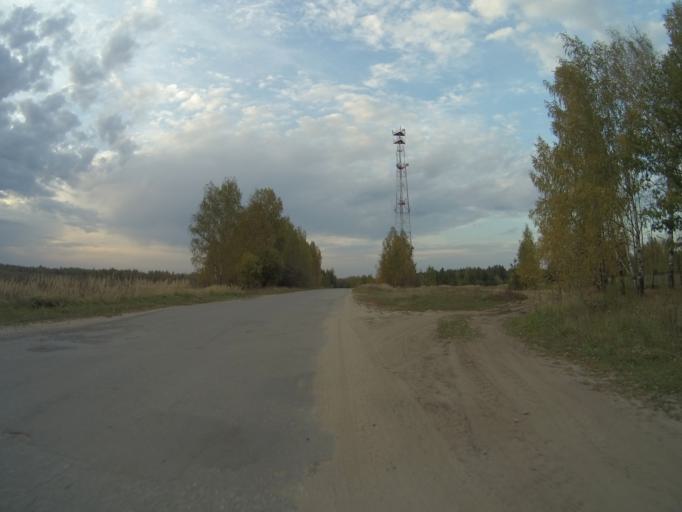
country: RU
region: Vladimir
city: Sobinka
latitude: 55.8767
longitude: 40.0970
